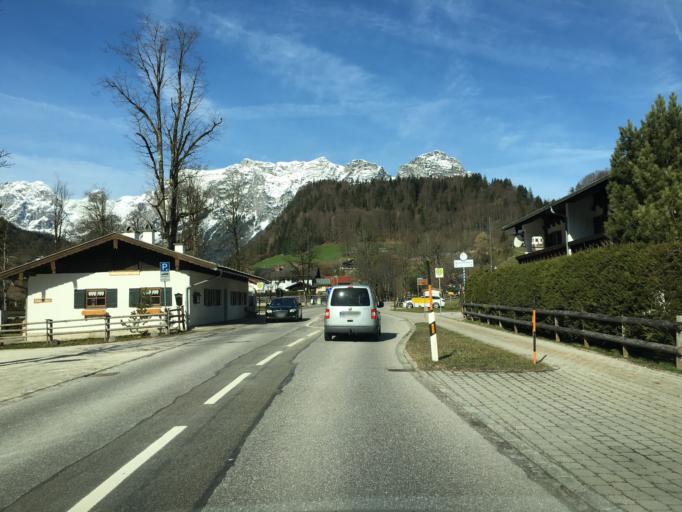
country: DE
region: Bavaria
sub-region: Upper Bavaria
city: Ramsau
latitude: 47.6069
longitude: 12.9026
